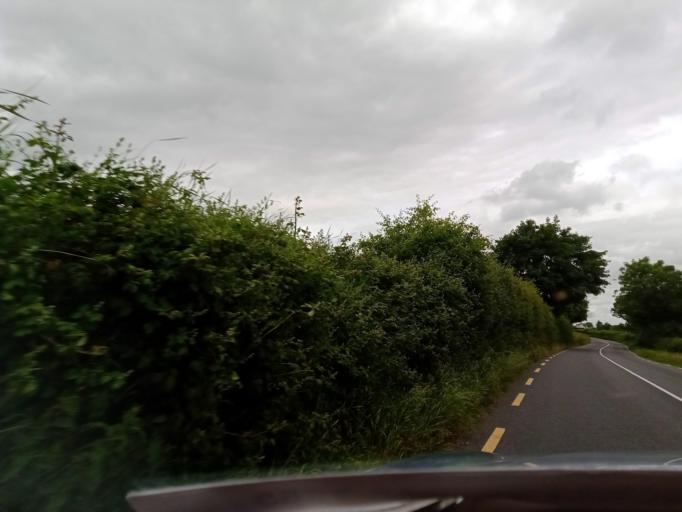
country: IE
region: Leinster
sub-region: Kilkenny
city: Thomastown
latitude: 52.4758
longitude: -7.2598
